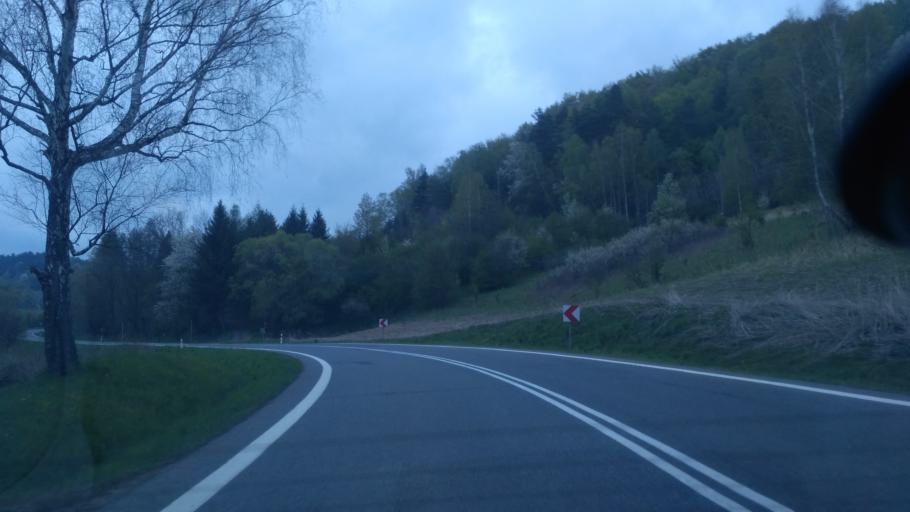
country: PL
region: Subcarpathian Voivodeship
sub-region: Powiat sanocki
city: Zagorz
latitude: 49.5384
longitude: 22.3040
